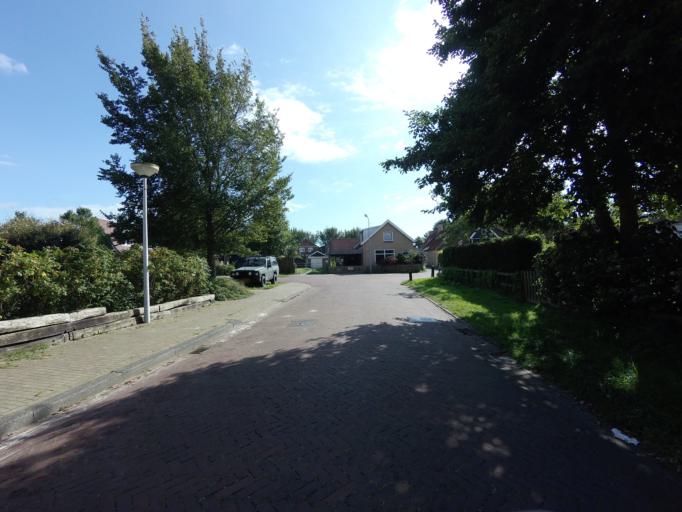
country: NL
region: Friesland
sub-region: Gemeente Terschelling
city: West-Terschelling
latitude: 53.3839
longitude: 5.2858
